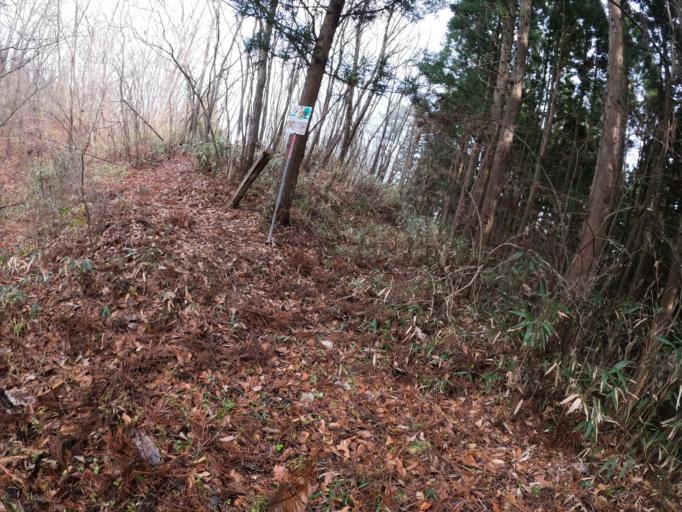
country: JP
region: Iwate
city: Ichinoseki
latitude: 38.8823
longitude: 141.1308
